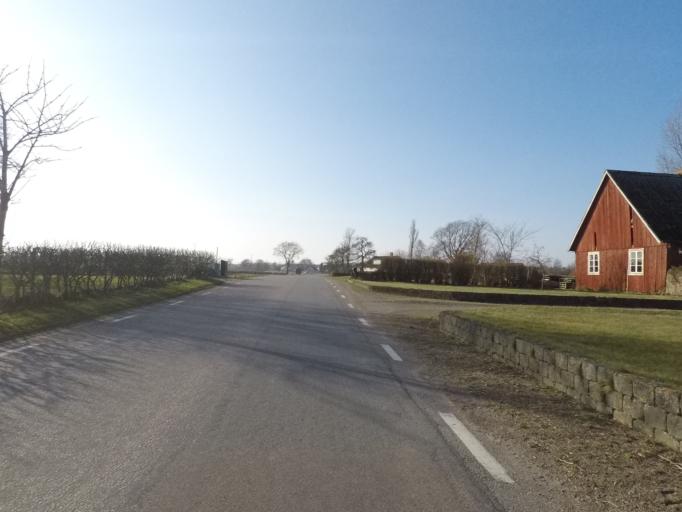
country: SE
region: Skane
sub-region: Hoganas Kommun
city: Hoganas
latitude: 56.2408
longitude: 12.6506
